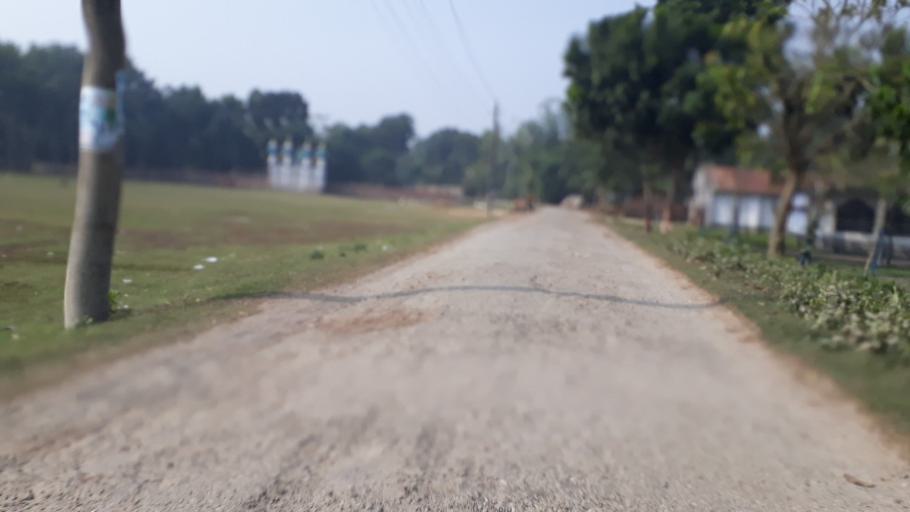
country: BD
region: Khulna
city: Kaliganj
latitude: 23.3511
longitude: 88.8986
